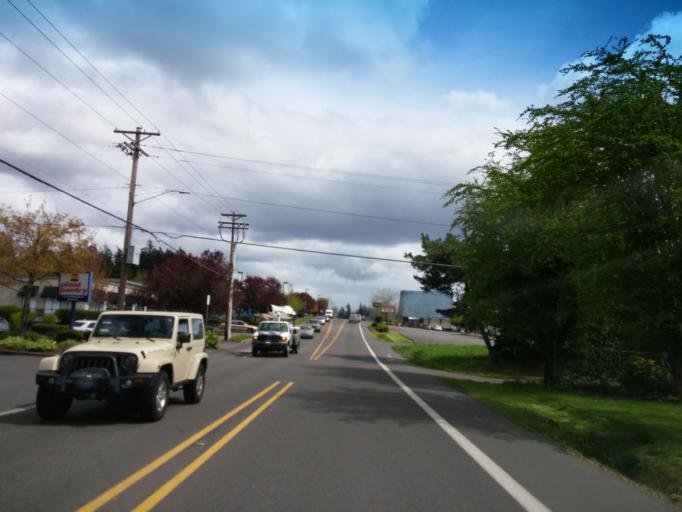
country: US
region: Oregon
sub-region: Washington County
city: Cedar Hills
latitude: 45.5027
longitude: -122.8095
